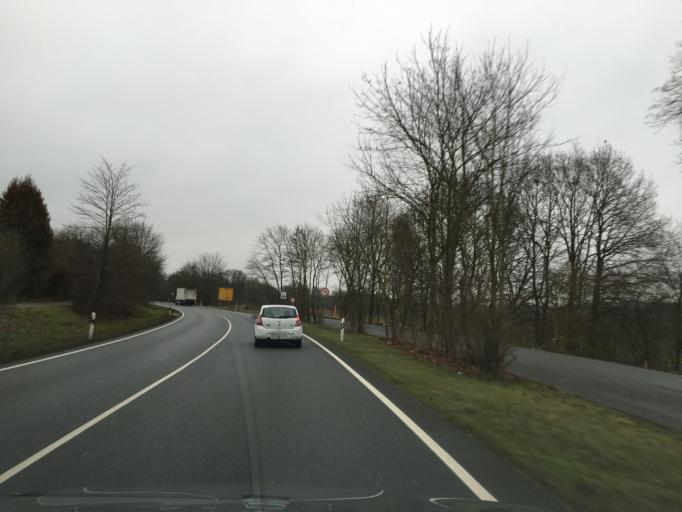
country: DE
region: Bavaria
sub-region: Regierungsbezirk Mittelfranken
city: Neunkirchen am Sand
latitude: 49.5166
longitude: 11.3302
